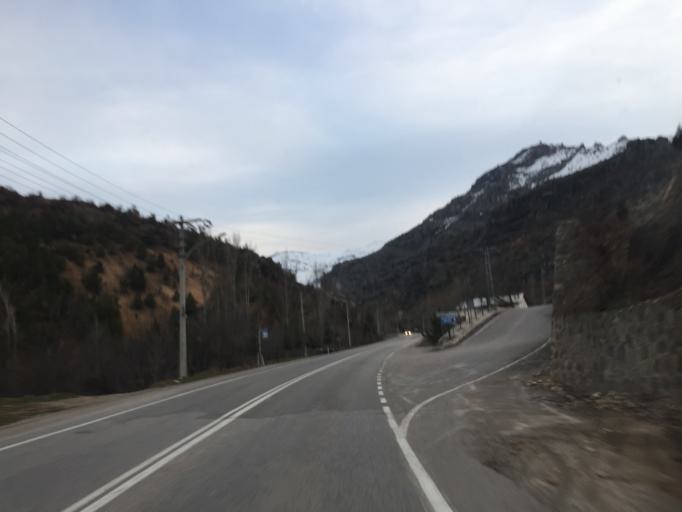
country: TR
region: Gumushane
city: Gumushkhane
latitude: 40.4801
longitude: 39.4624
